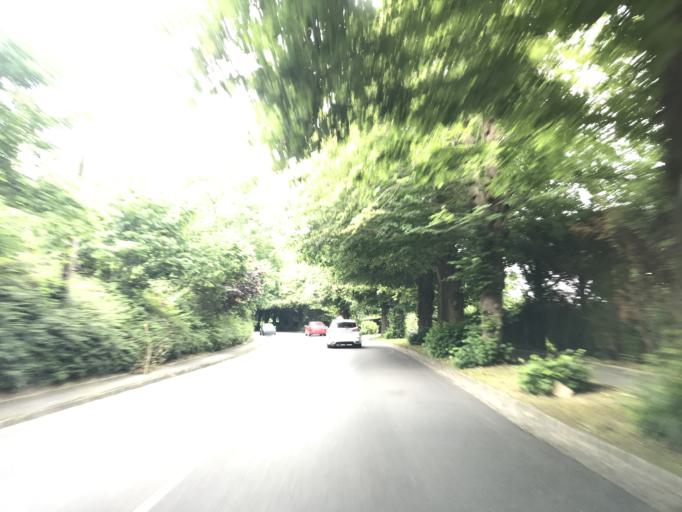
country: FR
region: Haute-Normandie
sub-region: Departement de la Seine-Maritime
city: Mont-Saint-Aignan
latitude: 49.4628
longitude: 1.0870
